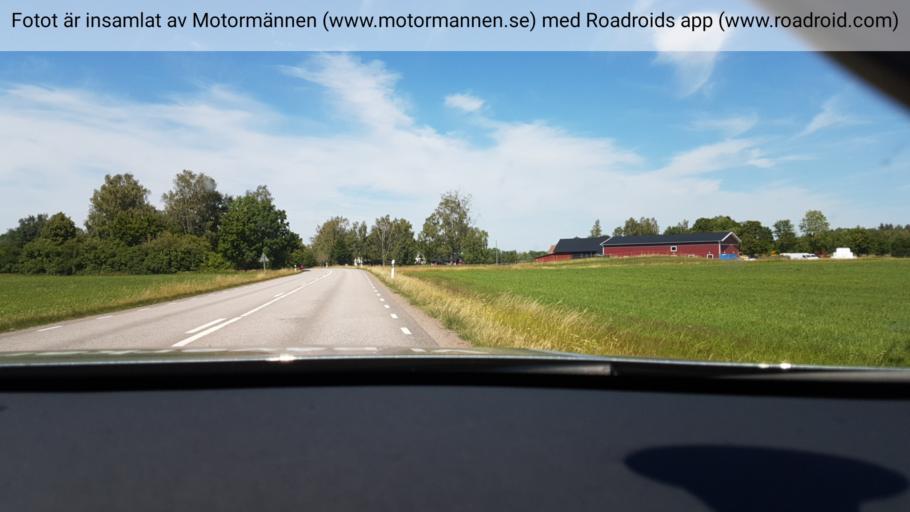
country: SE
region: Vaestra Goetaland
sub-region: Skovde Kommun
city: Stopen
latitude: 58.5074
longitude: 13.9713
